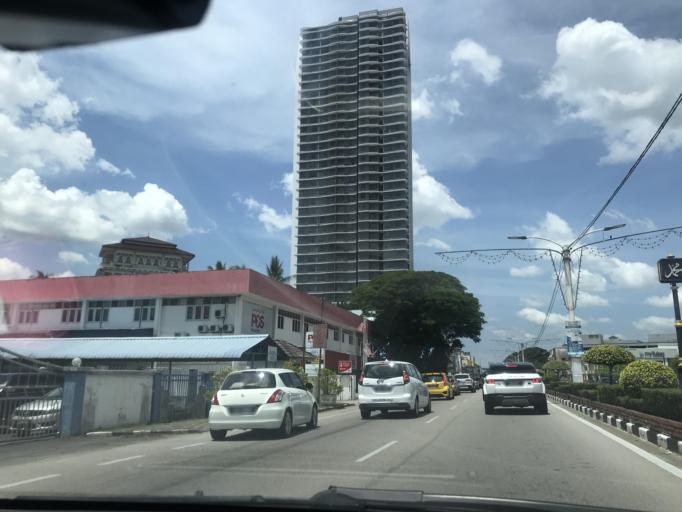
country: MY
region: Kelantan
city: Kota Bharu
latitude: 6.1219
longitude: 102.2396
